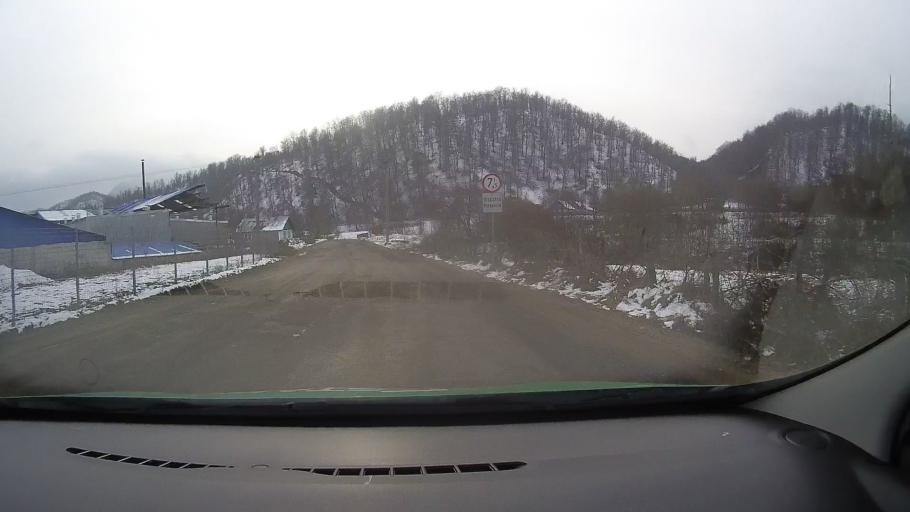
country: RO
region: Alba
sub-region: Oras Zlatna
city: Zlatna
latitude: 46.1201
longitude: 23.2058
